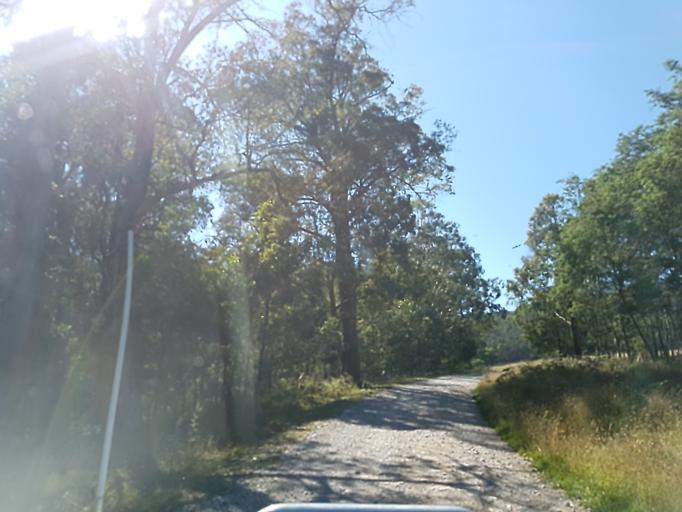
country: AU
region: Victoria
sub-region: East Gippsland
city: Lakes Entrance
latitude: -37.2325
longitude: 148.2774
